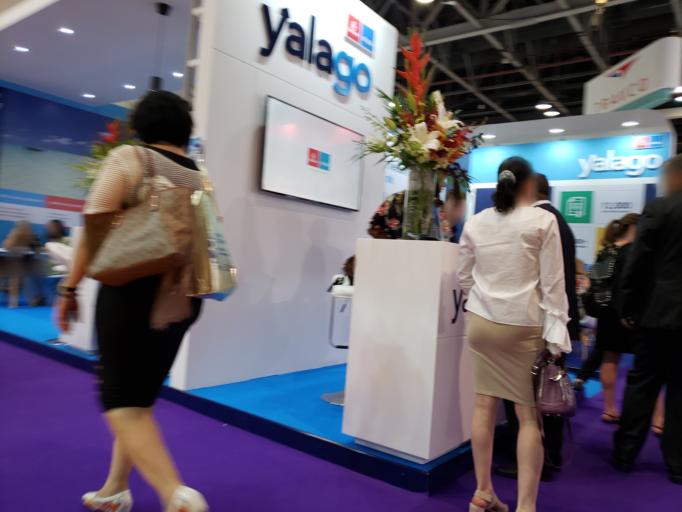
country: AE
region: Ash Shariqah
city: Sharjah
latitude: 25.2248
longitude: 55.2864
